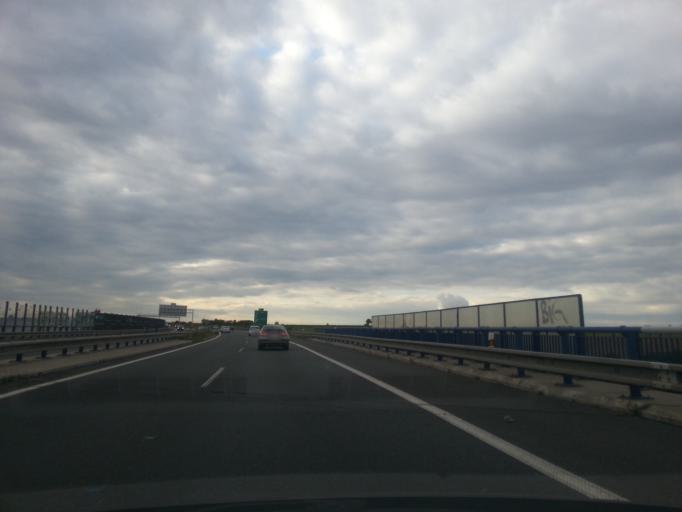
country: CZ
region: Central Bohemia
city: Hostivice
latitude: 50.0816
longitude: 14.2838
